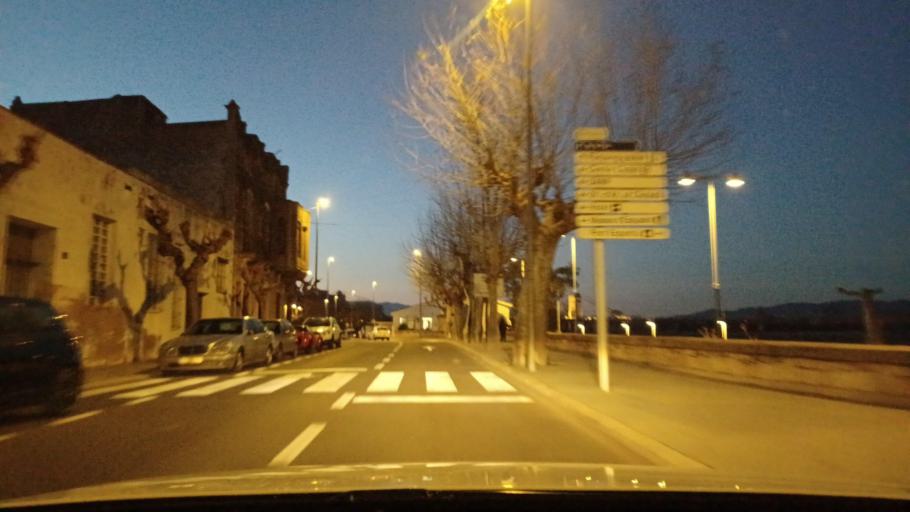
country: ES
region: Catalonia
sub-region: Provincia de Tarragona
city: Amposta
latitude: 40.7122
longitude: 0.5843
